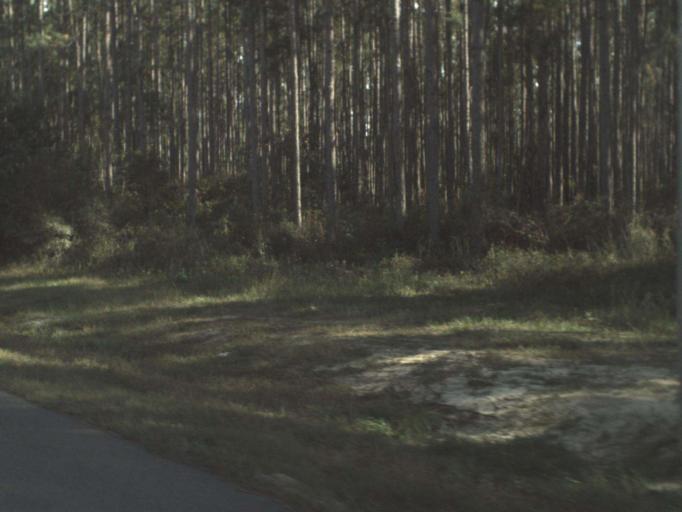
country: US
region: Florida
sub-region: Gadsden County
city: Midway
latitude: 30.4029
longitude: -84.5760
